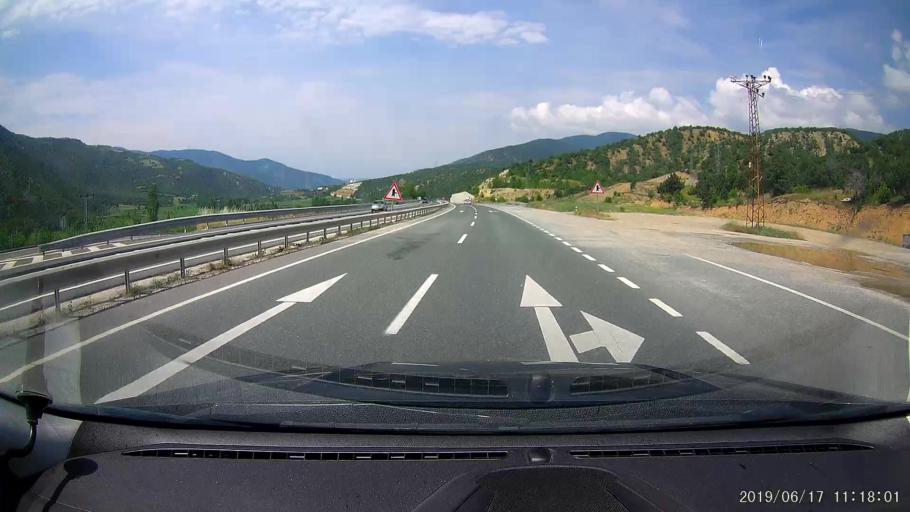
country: TR
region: Kastamonu
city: Tosya
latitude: 40.9388
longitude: 33.8603
